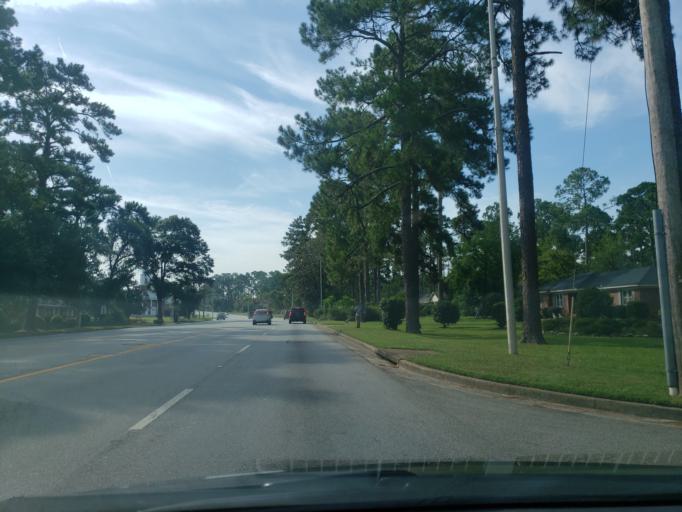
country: US
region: Georgia
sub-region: Dougherty County
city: Albany
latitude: 31.5926
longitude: -84.1927
